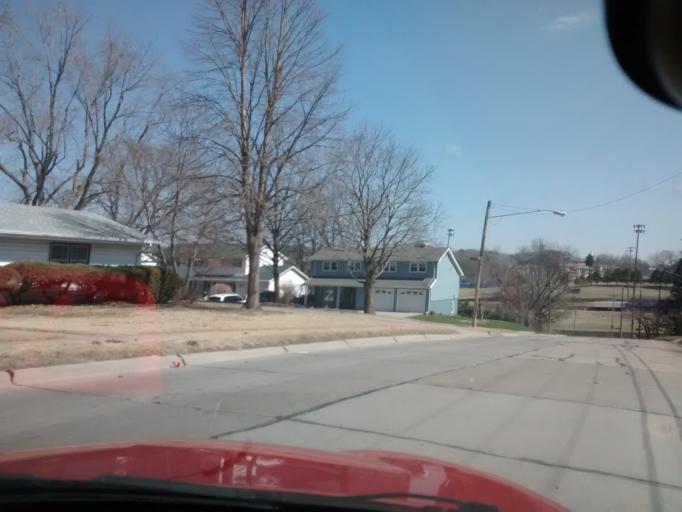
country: US
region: Nebraska
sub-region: Sarpy County
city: Bellevue
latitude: 41.1484
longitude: -95.9092
